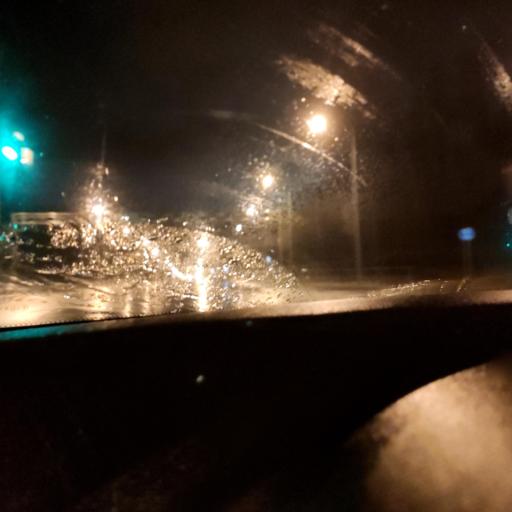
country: RU
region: Samara
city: Petra-Dubrava
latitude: 53.2955
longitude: 50.2455
